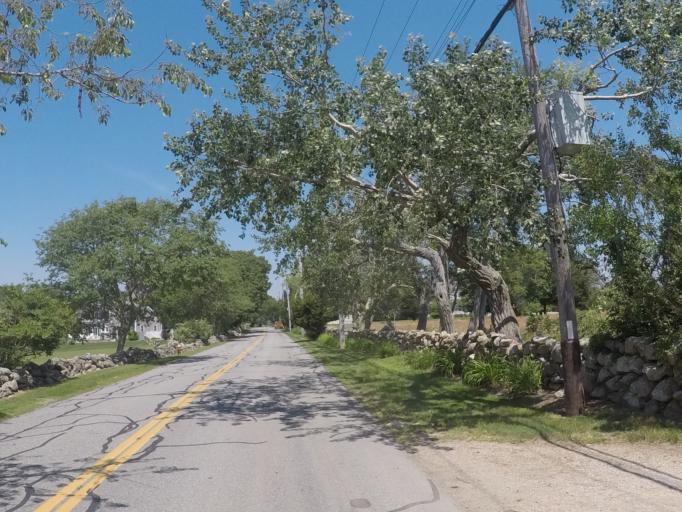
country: US
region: Massachusetts
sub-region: Bristol County
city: Bliss Corner
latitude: 41.5372
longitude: -70.9513
